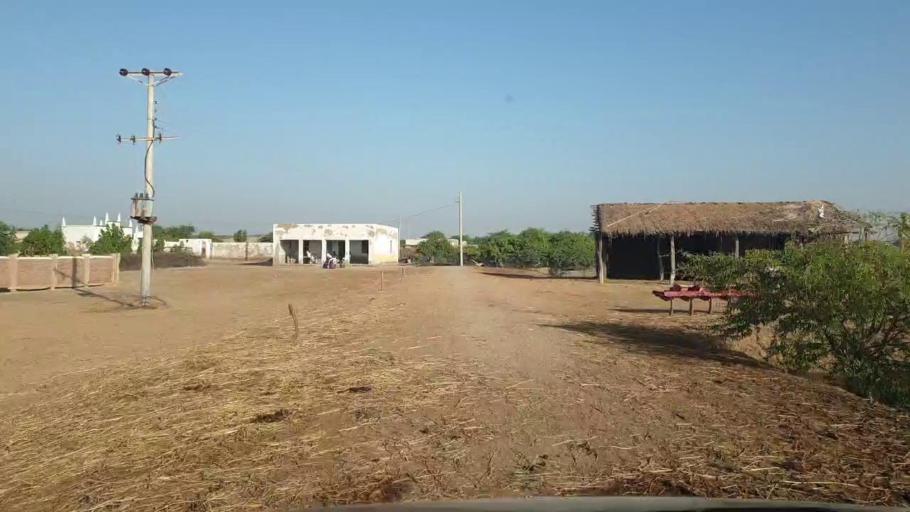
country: PK
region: Sindh
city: Badin
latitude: 24.7010
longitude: 68.8153
